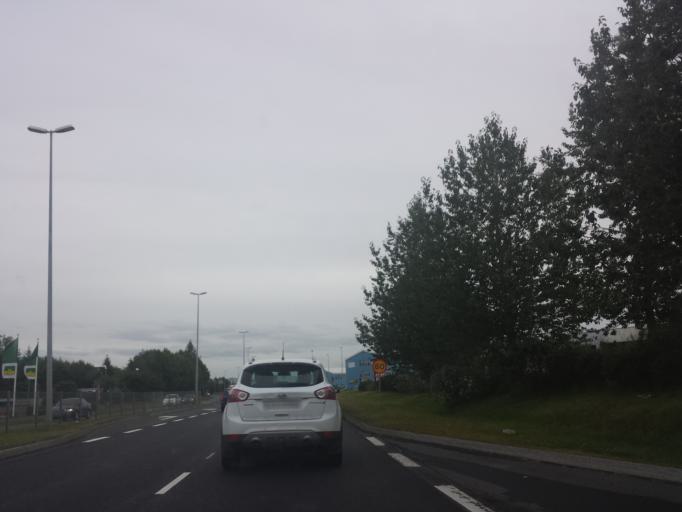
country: IS
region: Capital Region
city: Reykjavik
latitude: 64.1327
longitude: -21.8682
